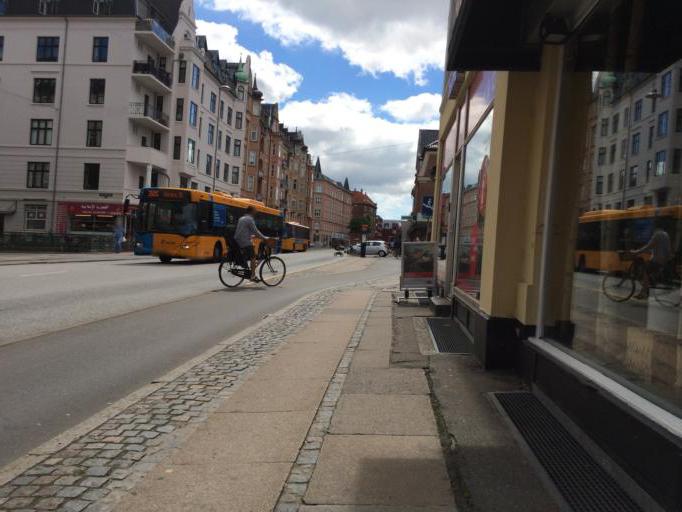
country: DK
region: Capital Region
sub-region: Kobenhavn
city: Christianshavn
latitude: 55.6554
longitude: 12.6098
